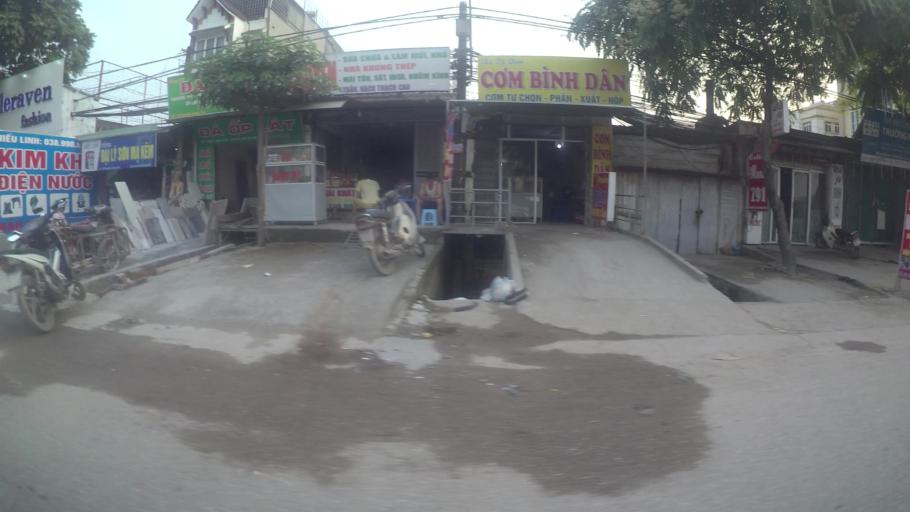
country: VN
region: Ha Noi
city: Tay Ho
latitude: 21.0781
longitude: 105.7890
